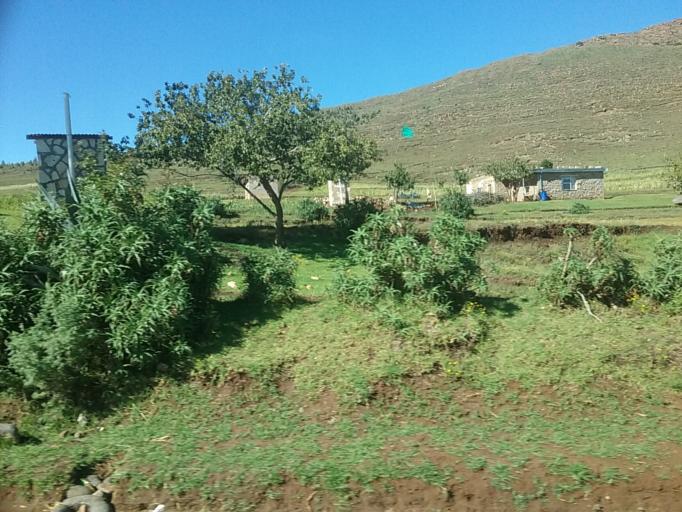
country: LS
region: Berea
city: Teyateyaneng
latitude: -29.2301
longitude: 27.8790
